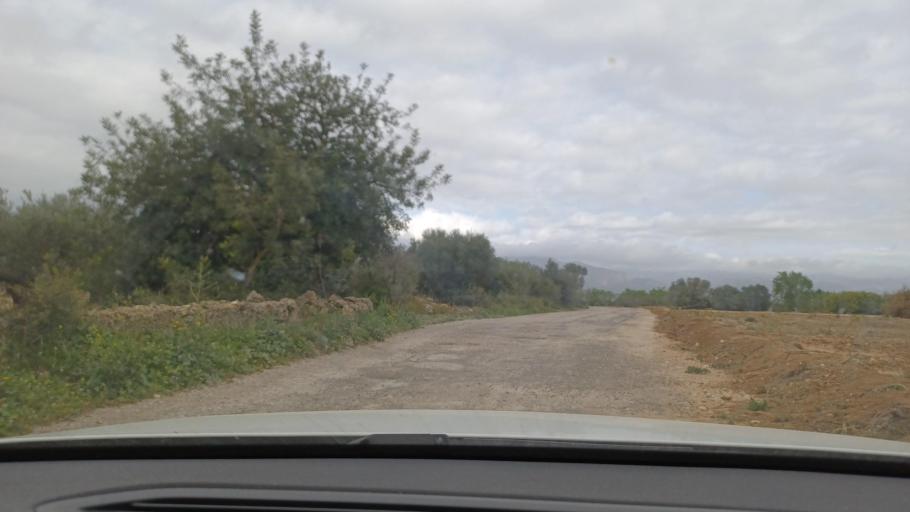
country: ES
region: Catalonia
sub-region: Provincia de Tarragona
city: Tortosa
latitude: 40.7905
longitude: 0.4768
